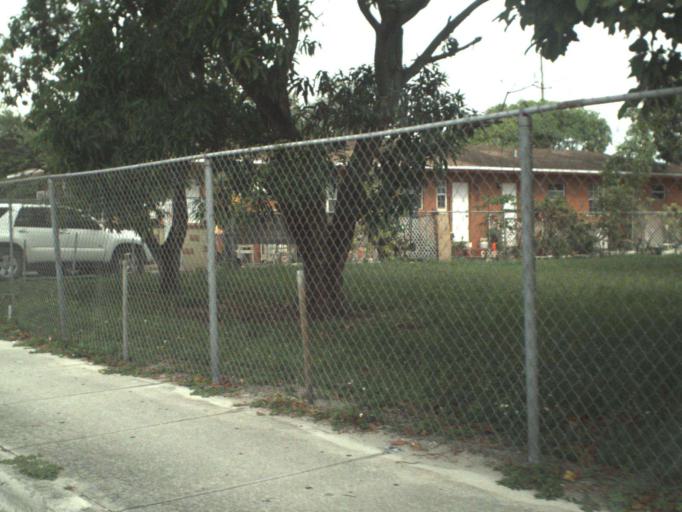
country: US
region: Florida
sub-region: Miami-Dade County
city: West Miami
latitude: 25.7713
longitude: -80.2771
